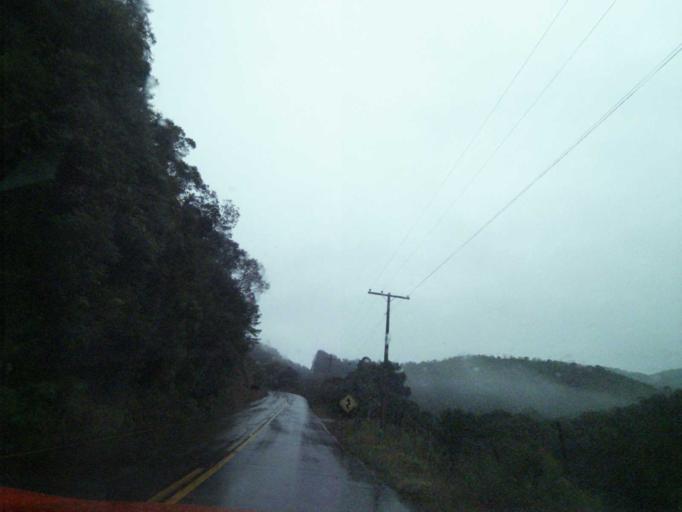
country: BR
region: Santa Catarina
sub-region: Anitapolis
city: Anitapolis
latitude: -27.8454
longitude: -49.0537
